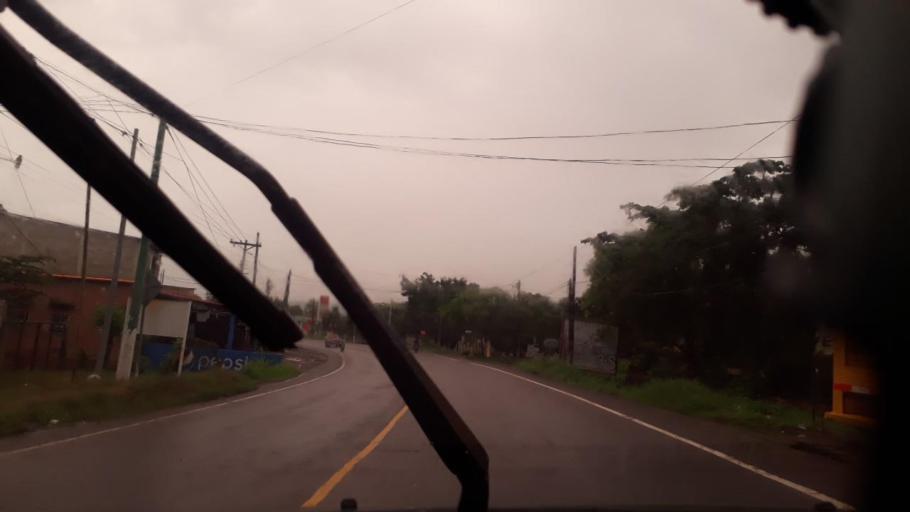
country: SV
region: Ahuachapan
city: San Francisco Menendez
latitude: 13.8800
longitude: -90.0976
